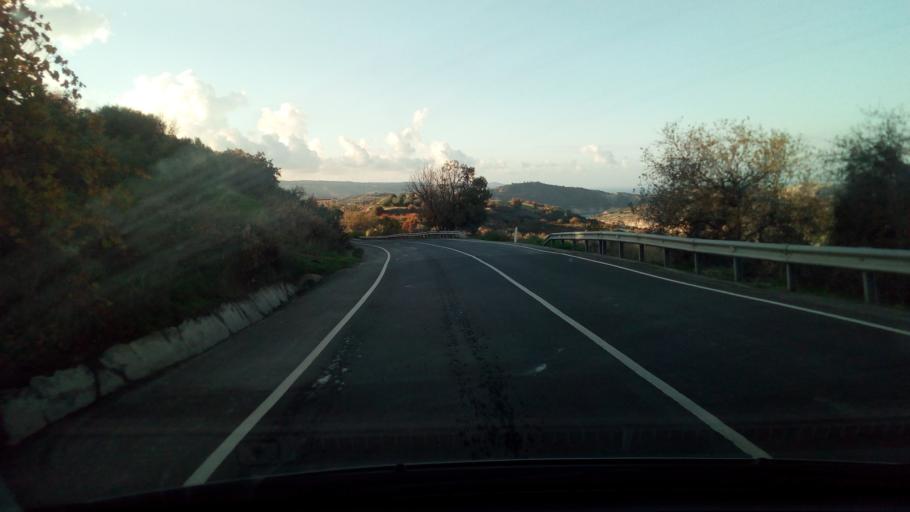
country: CY
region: Pafos
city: Polis
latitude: 34.9511
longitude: 32.4887
